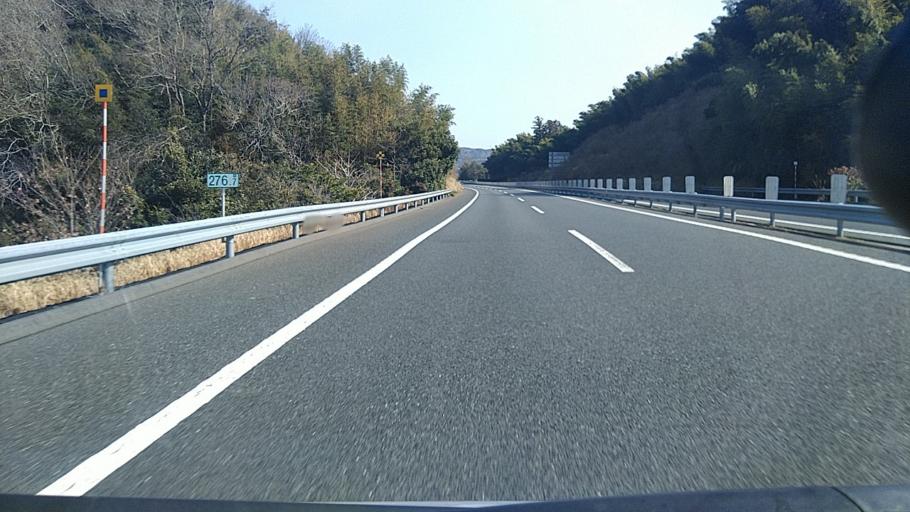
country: JP
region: Chiba
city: Kisarazu
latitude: 35.3578
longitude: 140.0331
